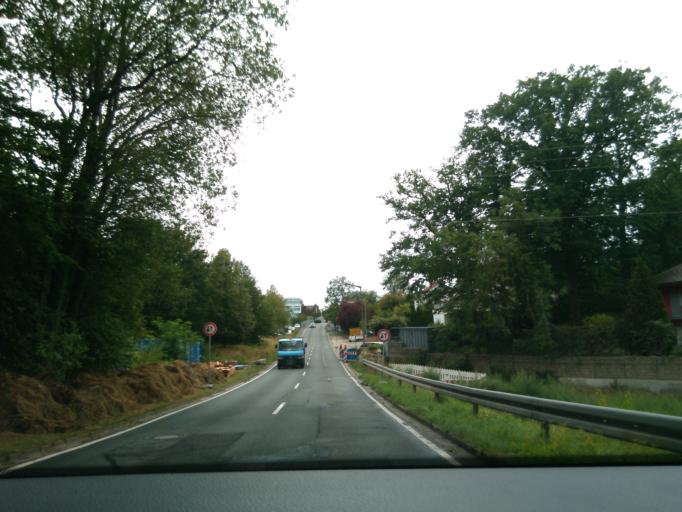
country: DE
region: Bavaria
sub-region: Regierungsbezirk Mittelfranken
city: Cadolzburg
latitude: 49.4580
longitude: 10.8694
